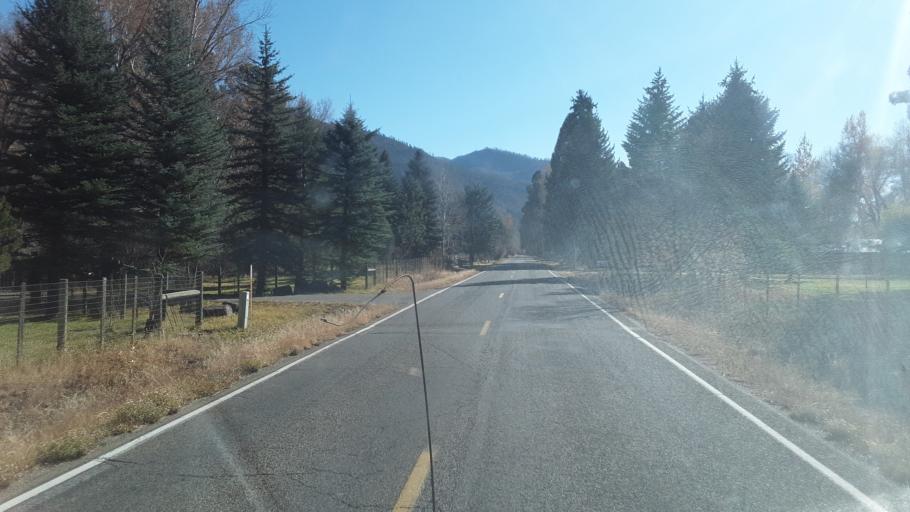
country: US
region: Colorado
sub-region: La Plata County
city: Durango
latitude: 37.4388
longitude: -107.7995
